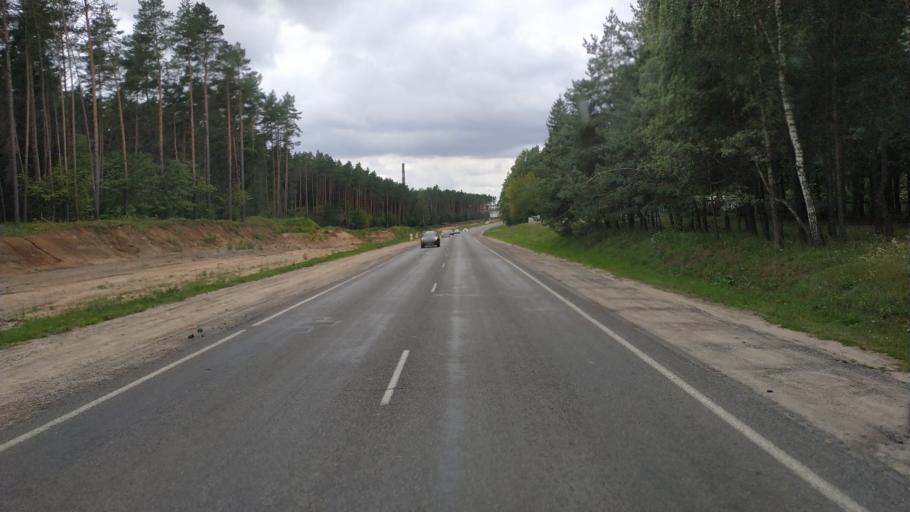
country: BY
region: Mogilev
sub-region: Mahilyowski Rayon
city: Veyno
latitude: 53.8769
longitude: 30.4214
